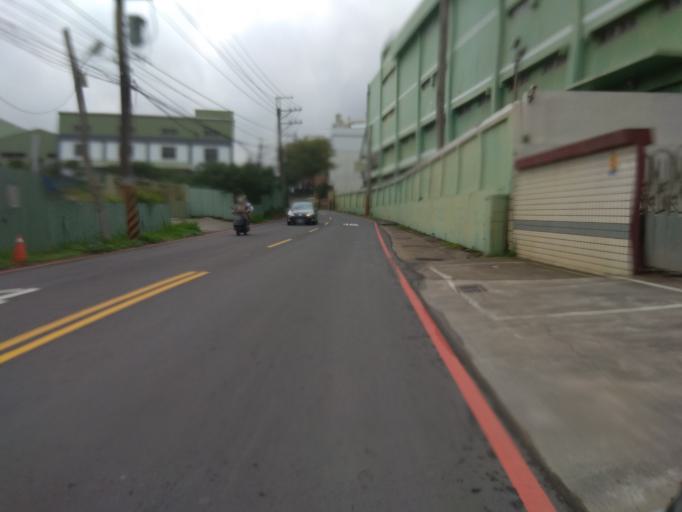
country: TW
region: Taiwan
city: Daxi
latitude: 24.9239
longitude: 121.1658
